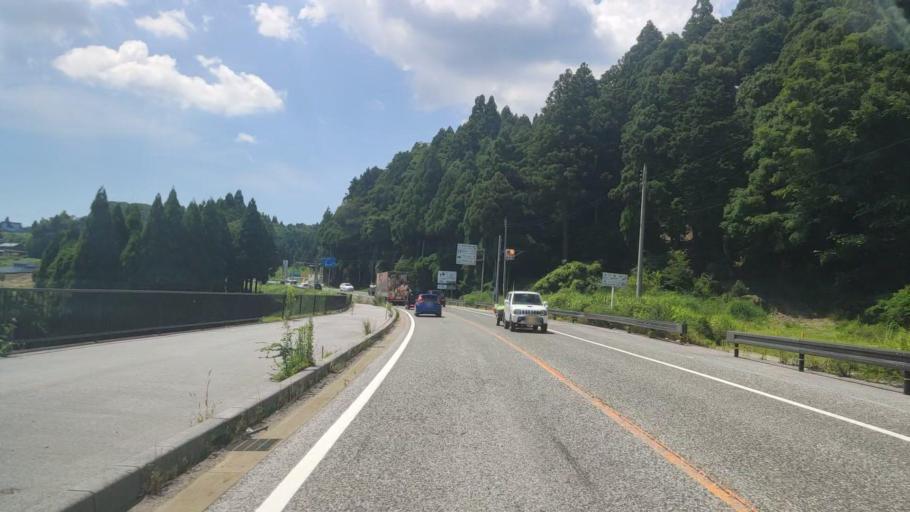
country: JP
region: Gifu
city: Tarui
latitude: 35.3800
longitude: 136.4365
